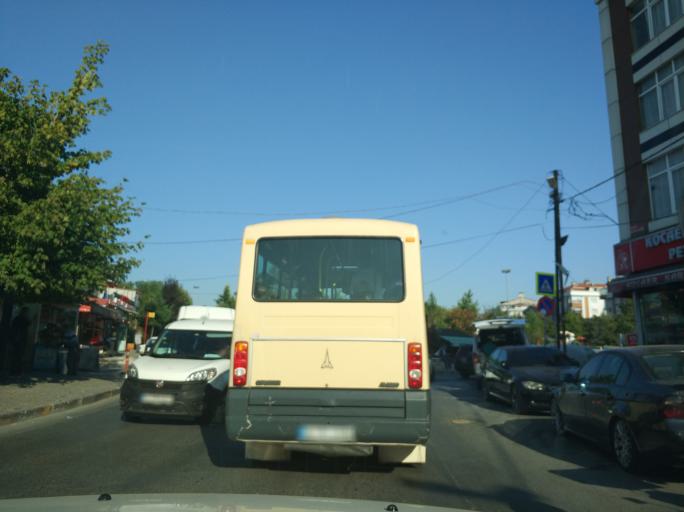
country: TR
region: Istanbul
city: Sultangazi
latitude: 41.0815
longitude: 28.9198
